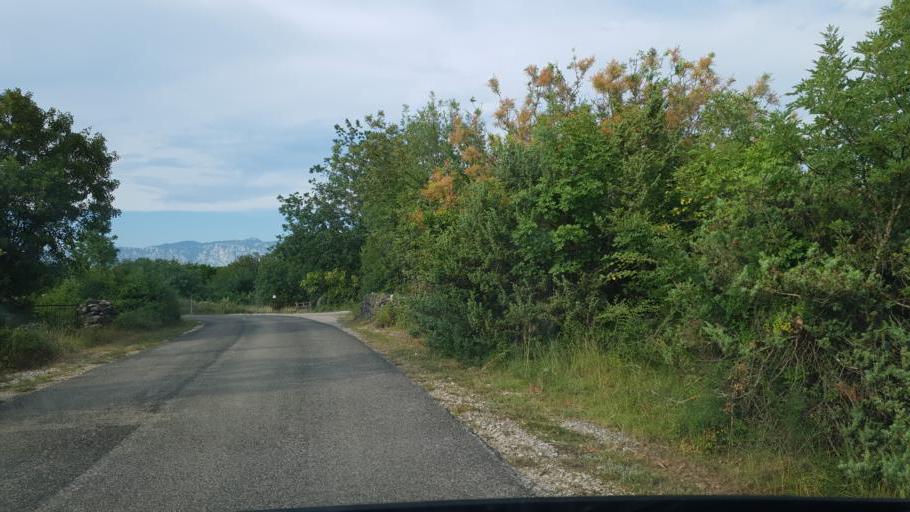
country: HR
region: Primorsko-Goranska
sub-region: Grad Crikvenica
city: Jadranovo
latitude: 45.1729
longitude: 14.6059
